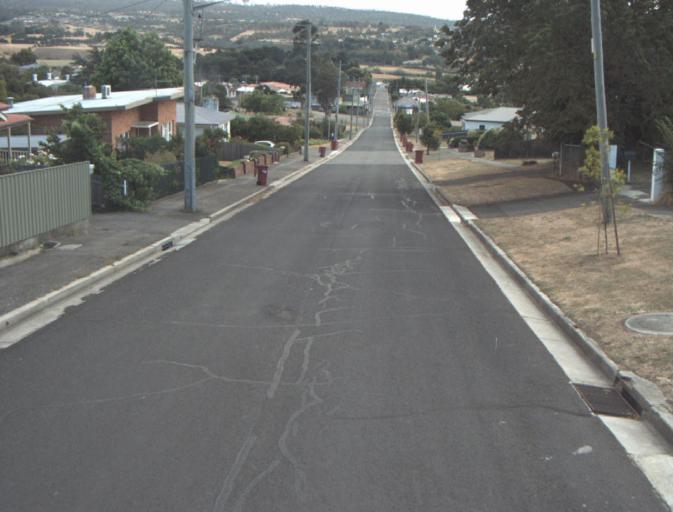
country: AU
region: Tasmania
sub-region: Launceston
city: Newstead
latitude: -41.4565
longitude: 147.2044
